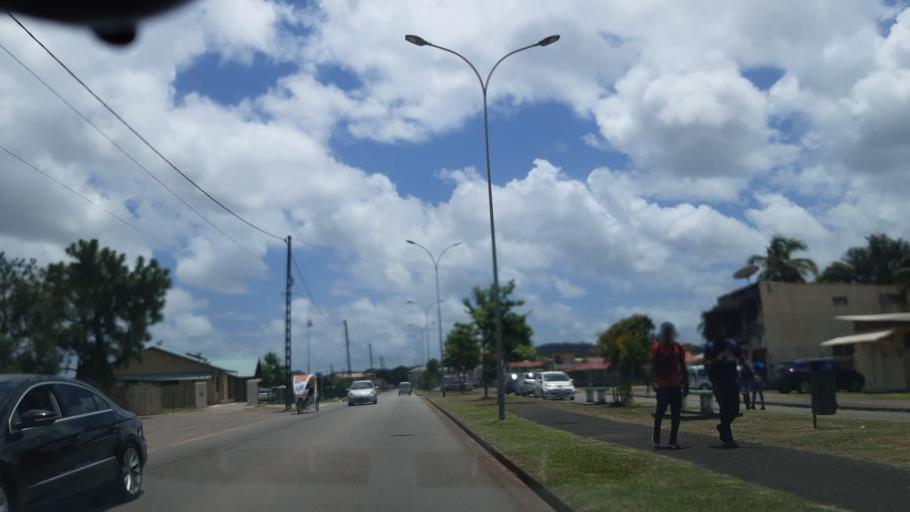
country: GF
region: Guyane
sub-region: Guyane
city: Cayenne
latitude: 4.9371
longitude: -52.3216
